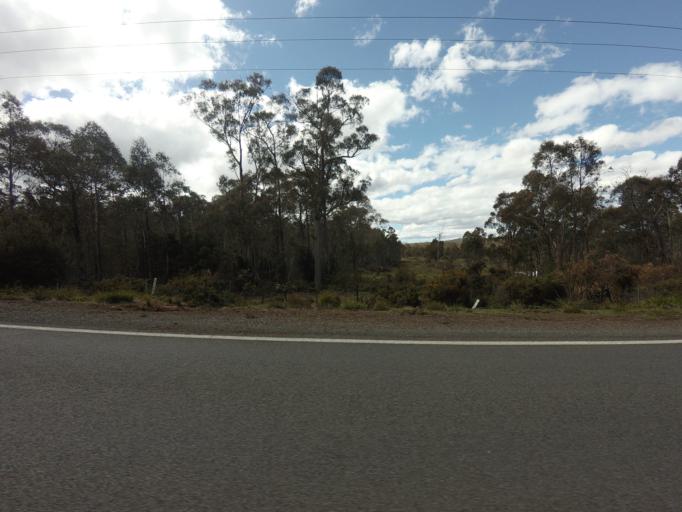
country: AU
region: Tasmania
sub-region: Northern Midlands
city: Evandale
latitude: -42.0251
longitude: 147.7634
